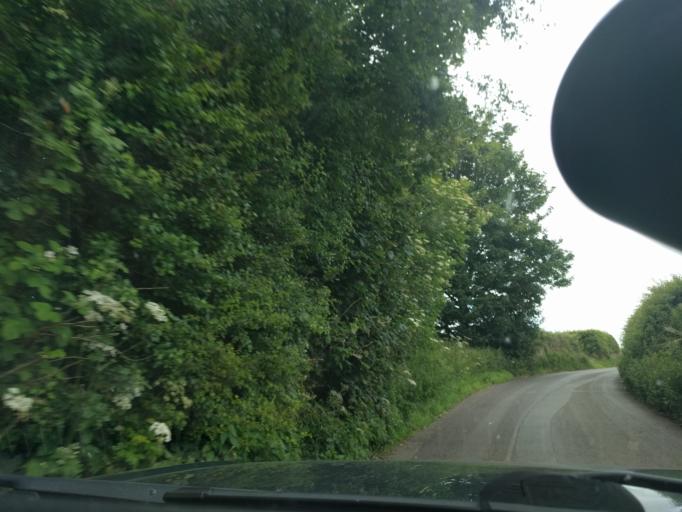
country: GB
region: England
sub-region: Wiltshire
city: Corsham
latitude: 51.4439
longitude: -2.1968
